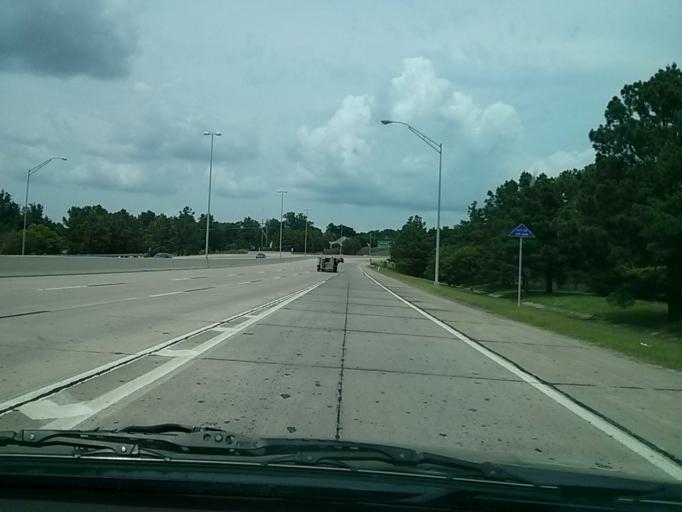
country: US
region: Oklahoma
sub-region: Tulsa County
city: Jenks
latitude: 36.0220
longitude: -95.9440
